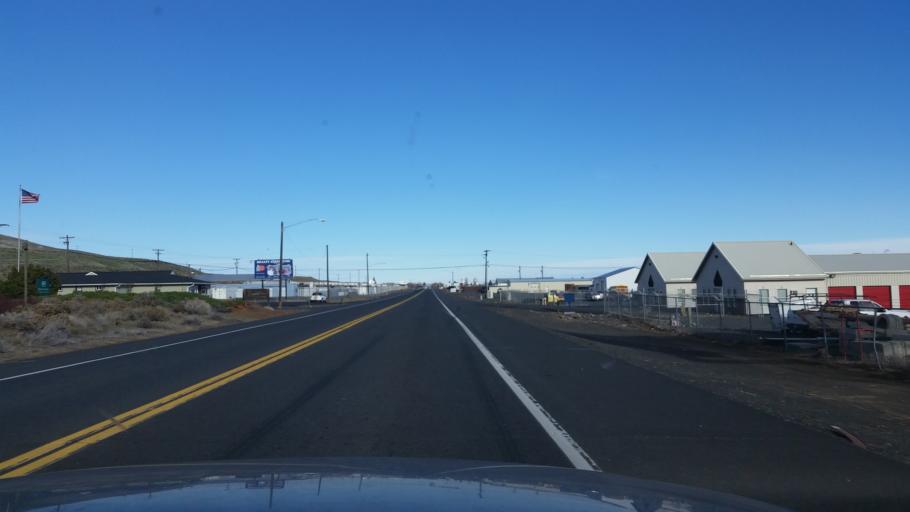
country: US
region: Washington
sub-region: Grant County
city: Ephrata
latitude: 47.2944
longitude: -119.5705
